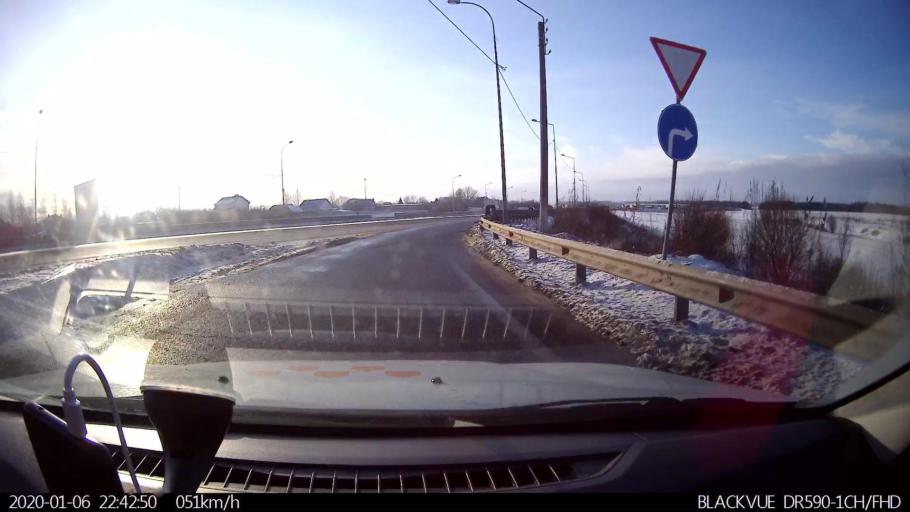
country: RU
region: Nizjnij Novgorod
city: Burevestnik
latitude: 56.1717
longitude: 43.7443
